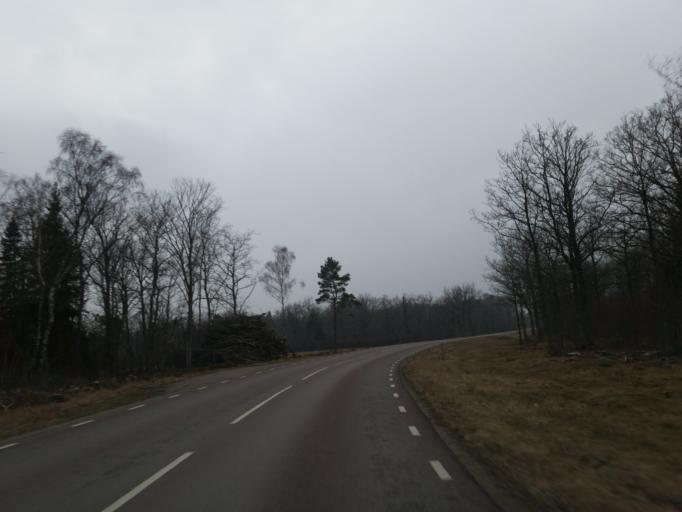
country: SE
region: Kalmar
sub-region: Morbylanga Kommun
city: Sodra Sandby
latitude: 56.6381
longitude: 16.5822
